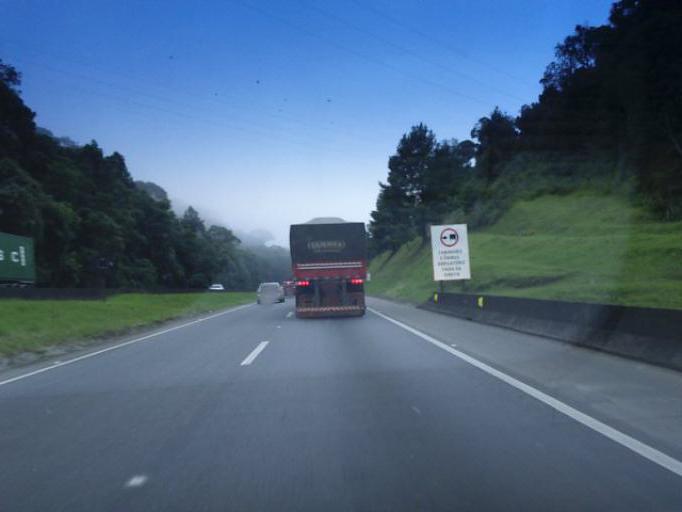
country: BR
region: Parana
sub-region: Sao Jose Dos Pinhais
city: Sao Jose dos Pinhais
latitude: -25.8540
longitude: -48.9819
